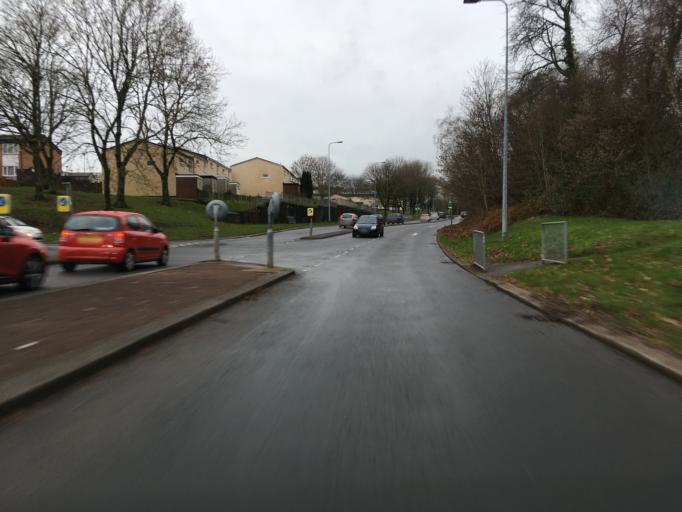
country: GB
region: Wales
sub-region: Cardiff
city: Cardiff
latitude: 51.5187
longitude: -3.1515
